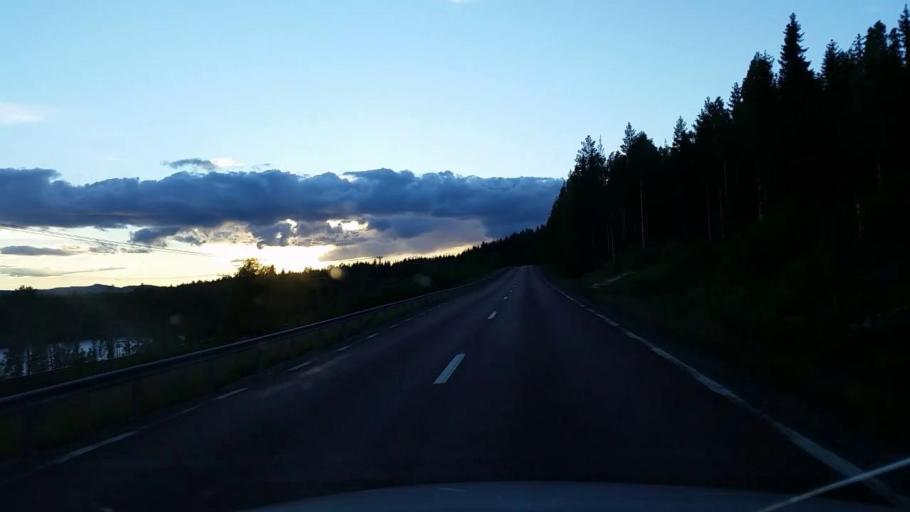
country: SE
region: Gaevleborg
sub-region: Ljusdals Kommun
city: Farila
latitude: 62.1062
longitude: 15.7729
